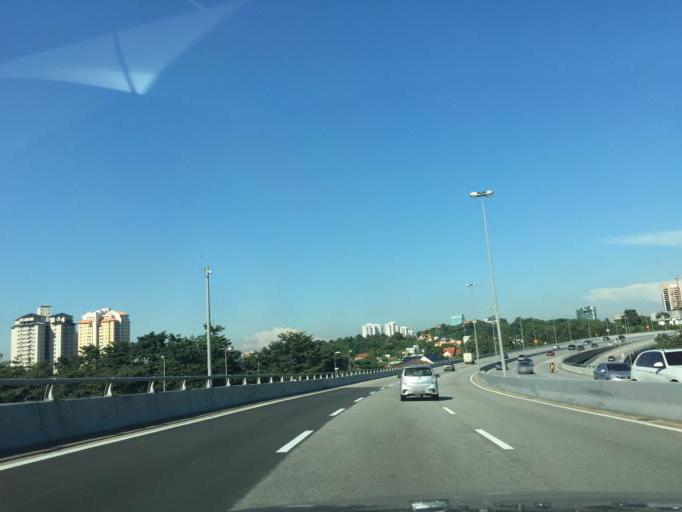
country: MY
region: Selangor
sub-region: Petaling
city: Petaling Jaya
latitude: 3.1599
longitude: 101.6277
